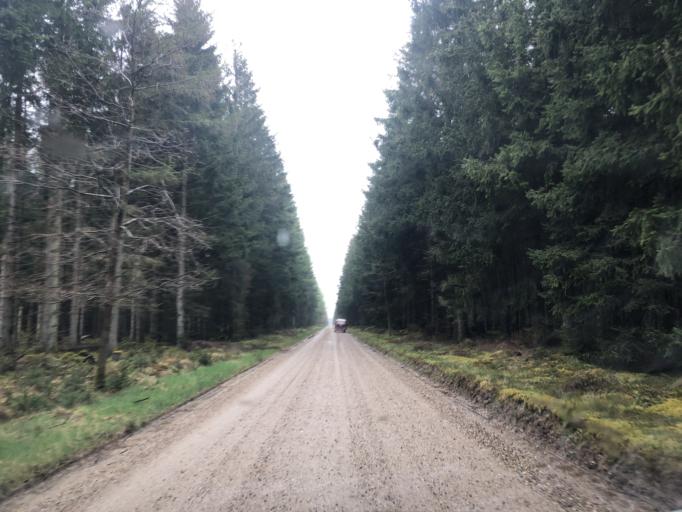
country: DK
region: Central Jutland
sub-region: Lemvig Kommune
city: Lemvig
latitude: 56.4655
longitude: 8.3941
